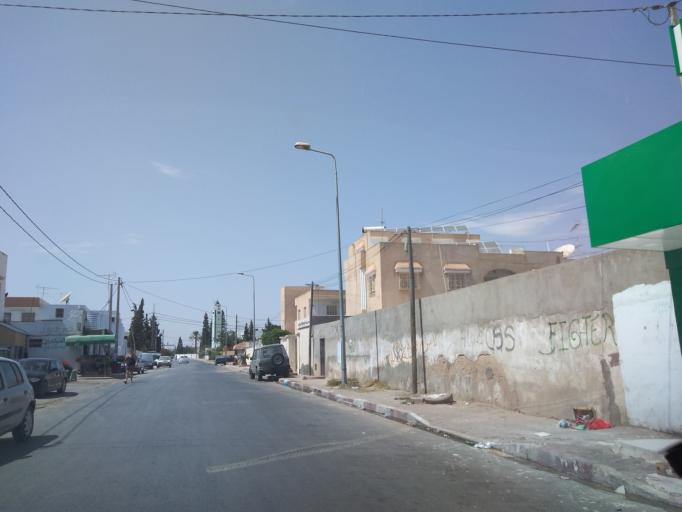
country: TN
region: Safaqis
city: Sfax
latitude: 34.7606
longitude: 10.7493
